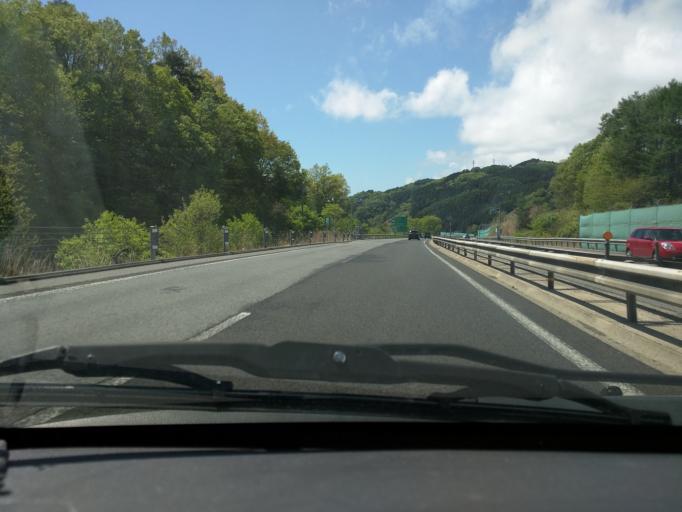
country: JP
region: Nagano
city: Nakano
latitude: 36.7891
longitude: 138.3212
